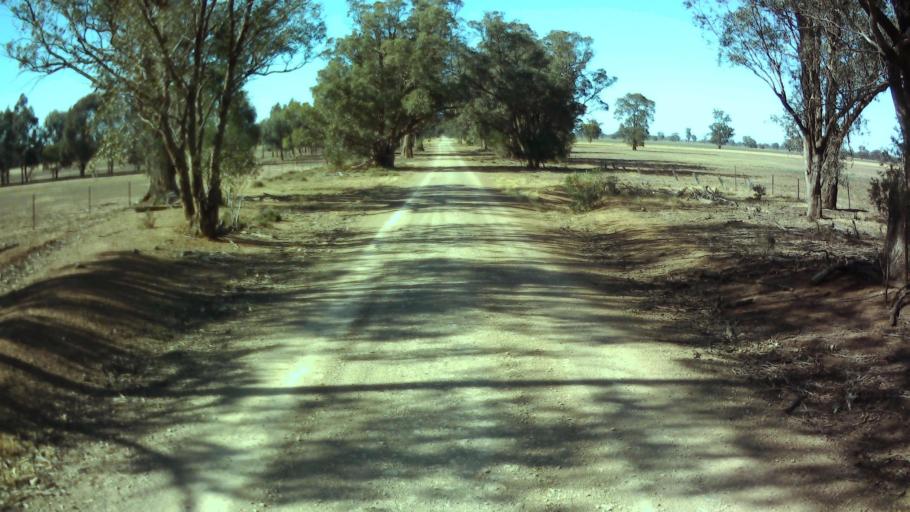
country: AU
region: New South Wales
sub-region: Weddin
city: Grenfell
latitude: -33.9289
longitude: 147.8733
